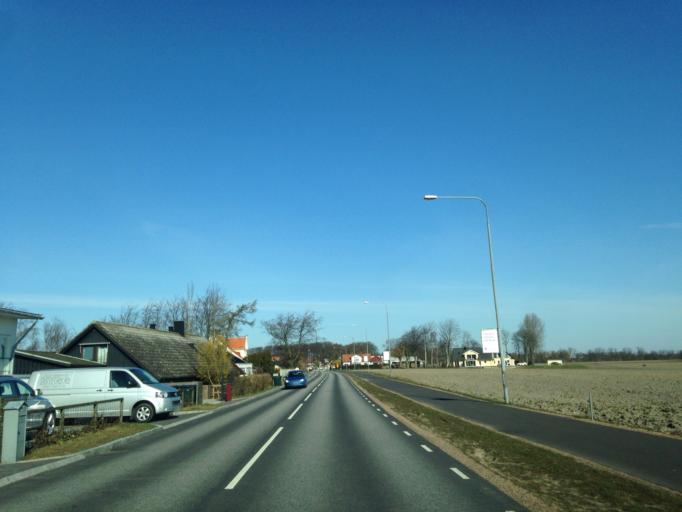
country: SE
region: Skane
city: Bjarred
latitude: 55.7048
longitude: 13.0402
